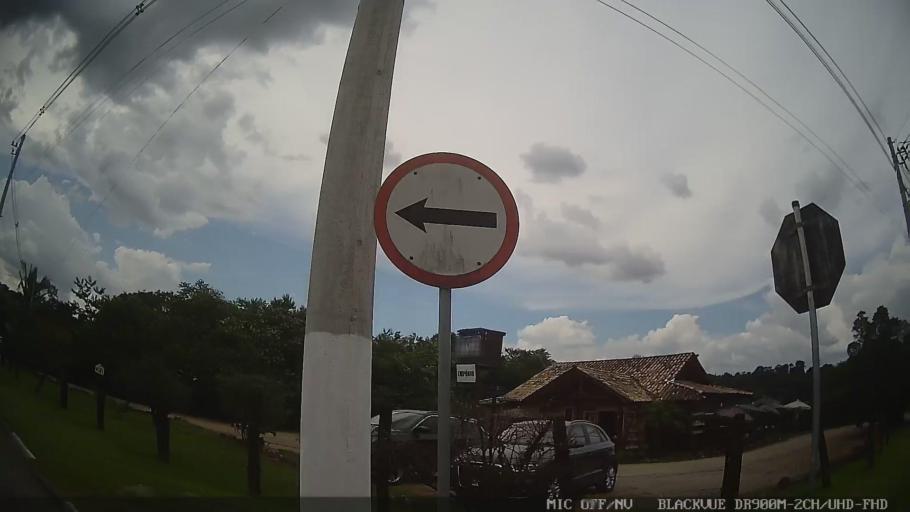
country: BR
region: Sao Paulo
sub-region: Atibaia
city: Atibaia
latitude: -23.1616
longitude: -46.5718
